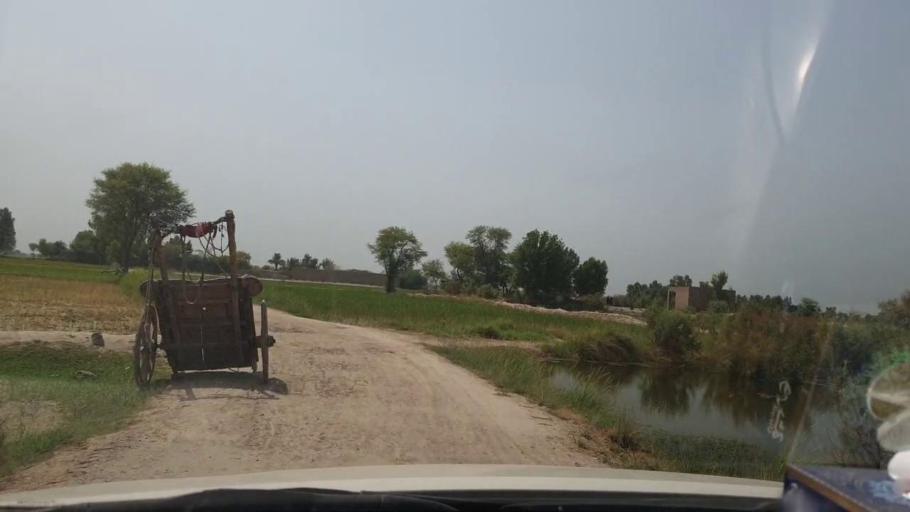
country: PK
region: Sindh
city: Shikarpur
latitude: 27.9845
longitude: 68.7069
